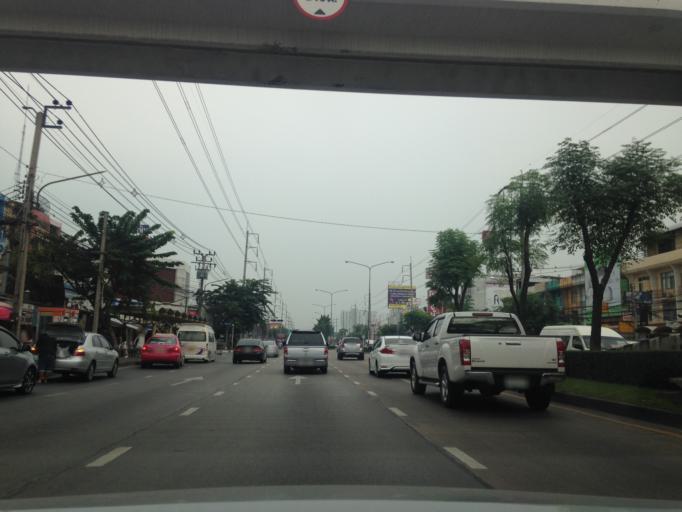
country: TH
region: Bangkok
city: Khan Na Yao
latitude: 13.8439
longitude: 100.6529
